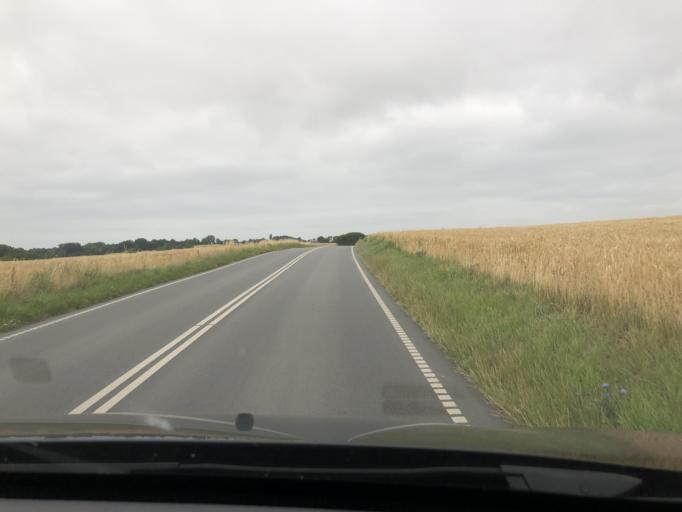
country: DK
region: South Denmark
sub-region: AEro Kommune
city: Marstal
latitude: 54.8422
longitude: 10.4780
